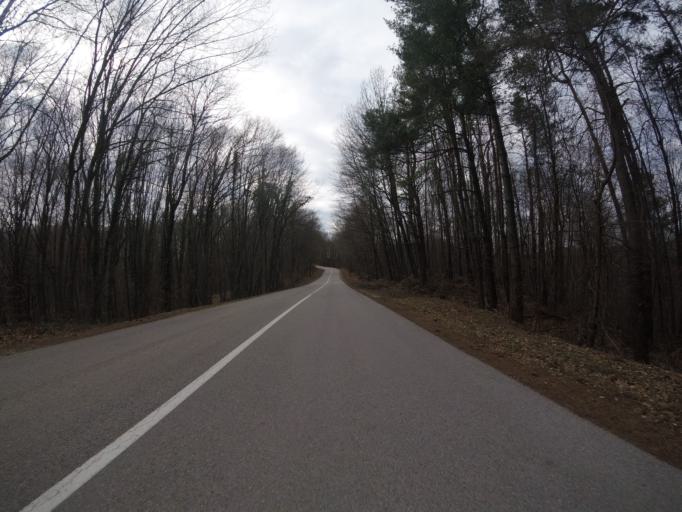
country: HR
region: Zagrebacka
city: Mraclin
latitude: 45.5359
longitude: 16.0581
